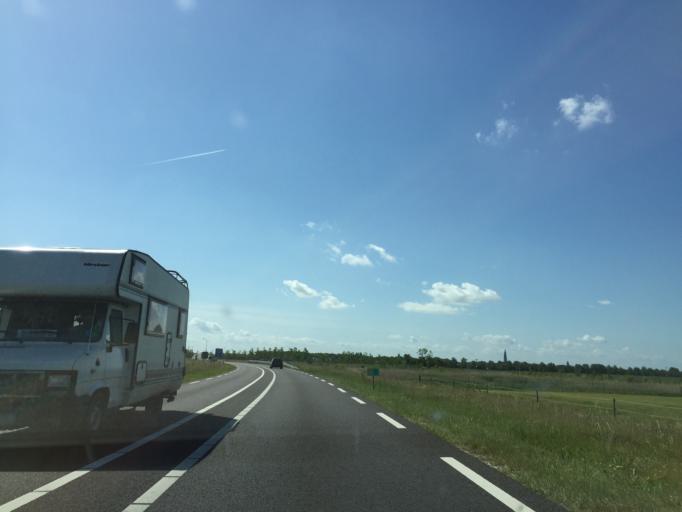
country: NL
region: Zeeland
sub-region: Gemeente Middelburg
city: Middelburg
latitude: 51.5239
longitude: 3.6149
